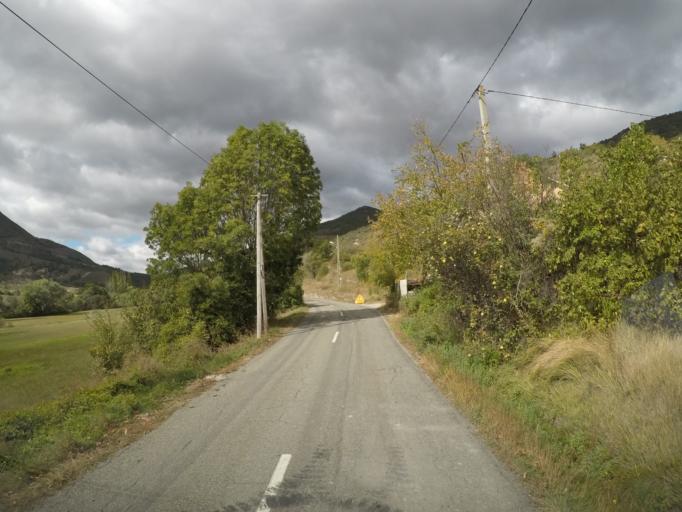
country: FR
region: Provence-Alpes-Cote d'Azur
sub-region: Departement du Vaucluse
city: Sault
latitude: 44.1757
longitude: 5.5898
